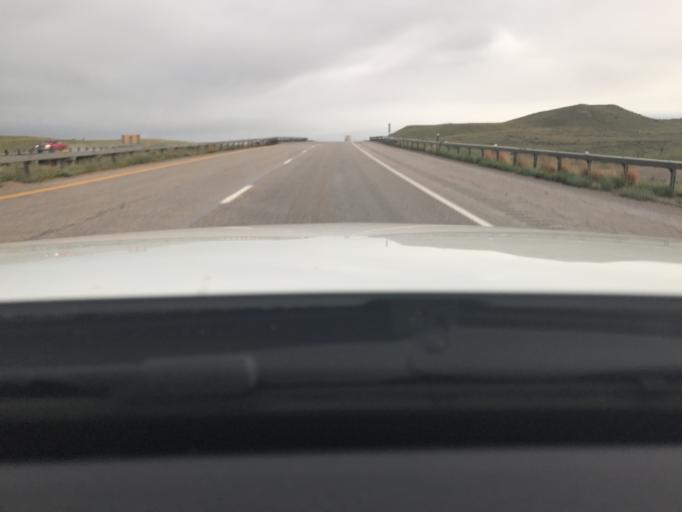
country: US
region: Wyoming
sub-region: Converse County
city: Glenrock
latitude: 42.8364
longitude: -105.8574
